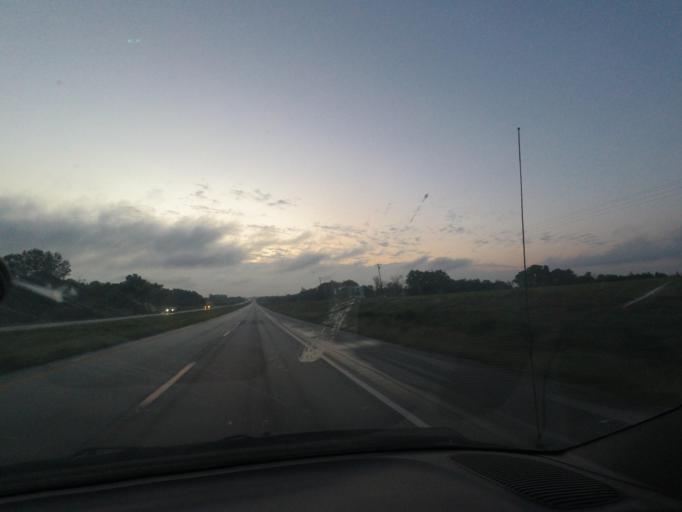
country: US
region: Missouri
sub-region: Linn County
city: Marceline
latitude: 39.7620
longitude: -93.0009
